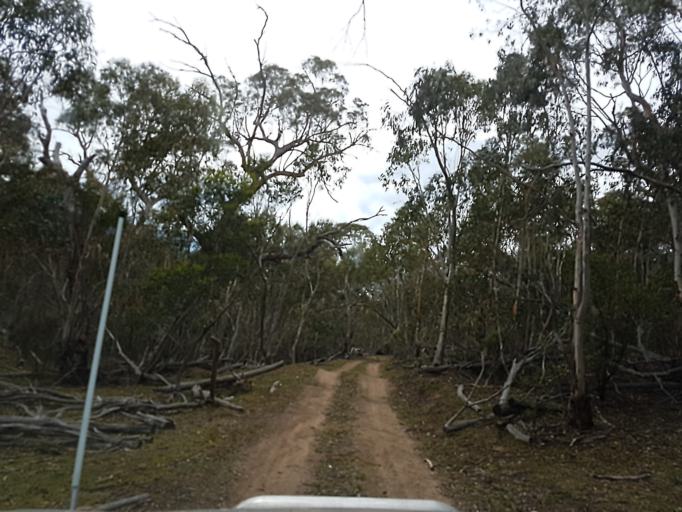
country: AU
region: New South Wales
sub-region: Snowy River
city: Jindabyne
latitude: -36.8507
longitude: 148.2556
